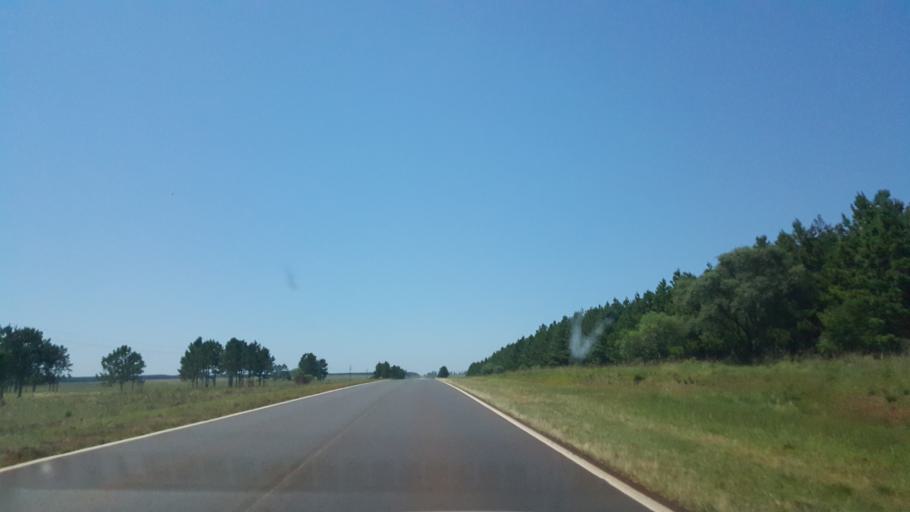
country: AR
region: Corrientes
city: Santo Tome
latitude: -28.3900
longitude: -56.1077
